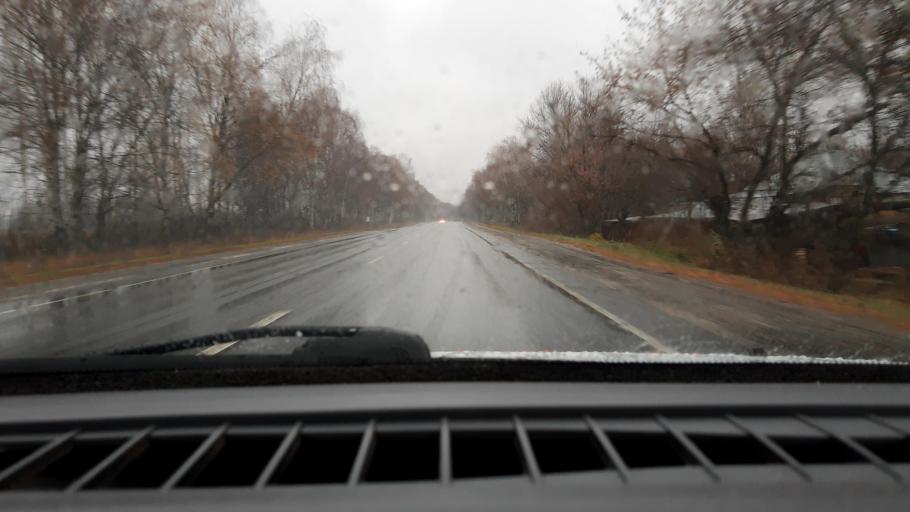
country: RU
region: Nizjnij Novgorod
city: Sitniki
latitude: 56.5309
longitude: 44.0241
